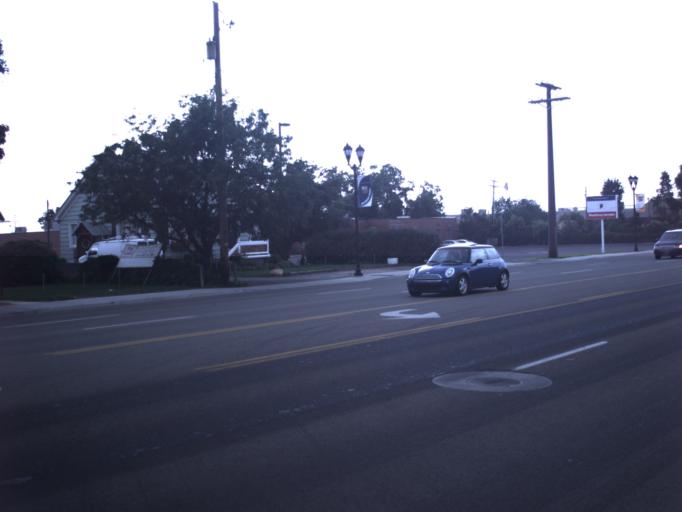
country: US
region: Utah
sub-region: Salt Lake County
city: Midvale
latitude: 40.6178
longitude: -111.8905
